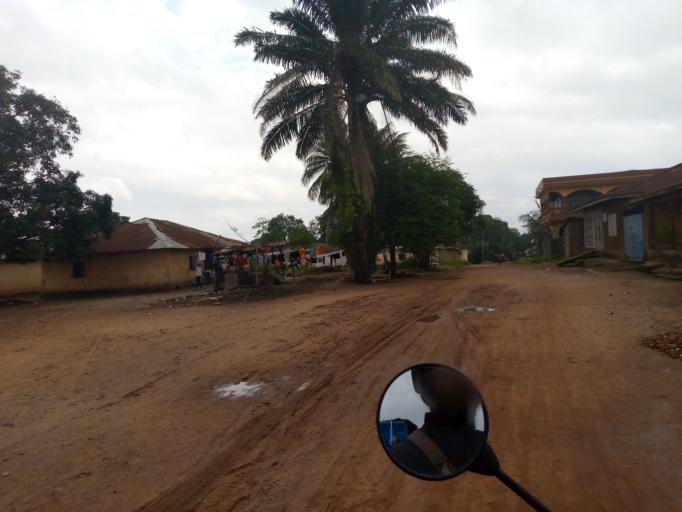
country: SL
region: Eastern Province
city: Kenema
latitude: 7.8629
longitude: -11.1953
